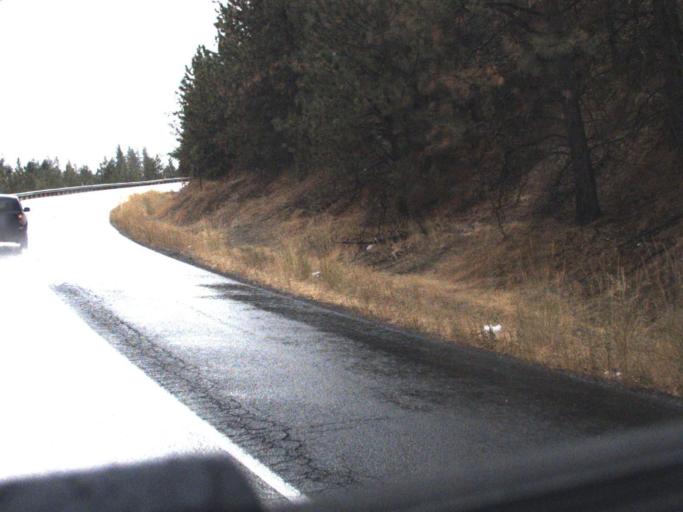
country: US
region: Washington
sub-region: Spokane County
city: Spokane
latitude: 47.5215
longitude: -117.3945
